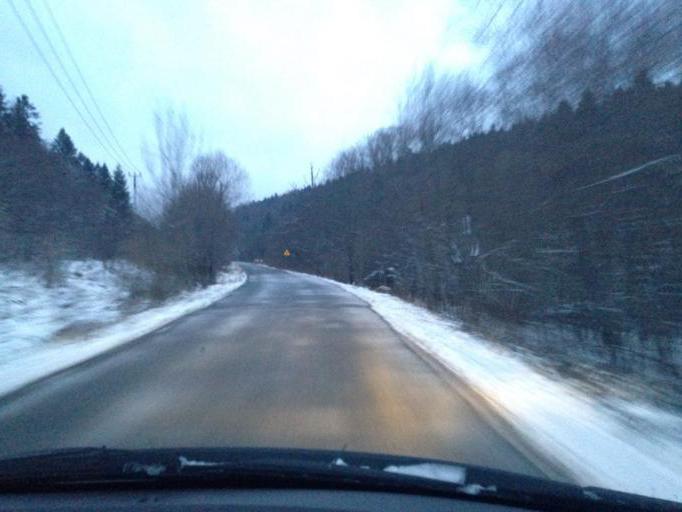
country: PL
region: Subcarpathian Voivodeship
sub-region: Powiat jasielski
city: Krempna
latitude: 49.5077
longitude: 21.5399
